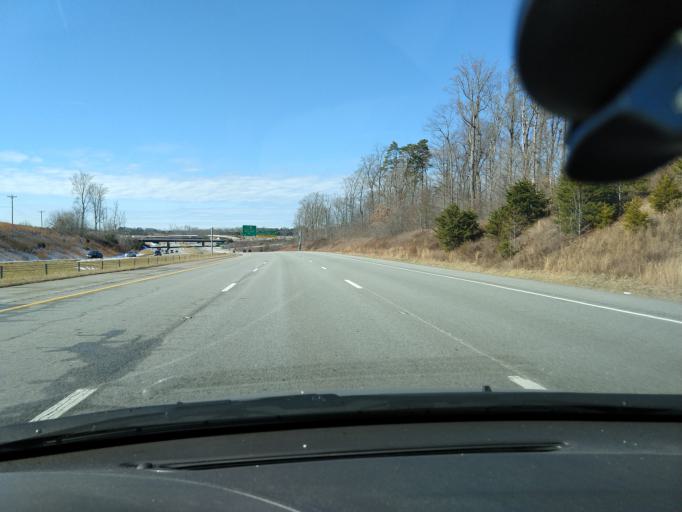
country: US
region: North Carolina
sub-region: Guilford County
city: Oak Ridge
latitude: 36.1213
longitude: -79.9217
